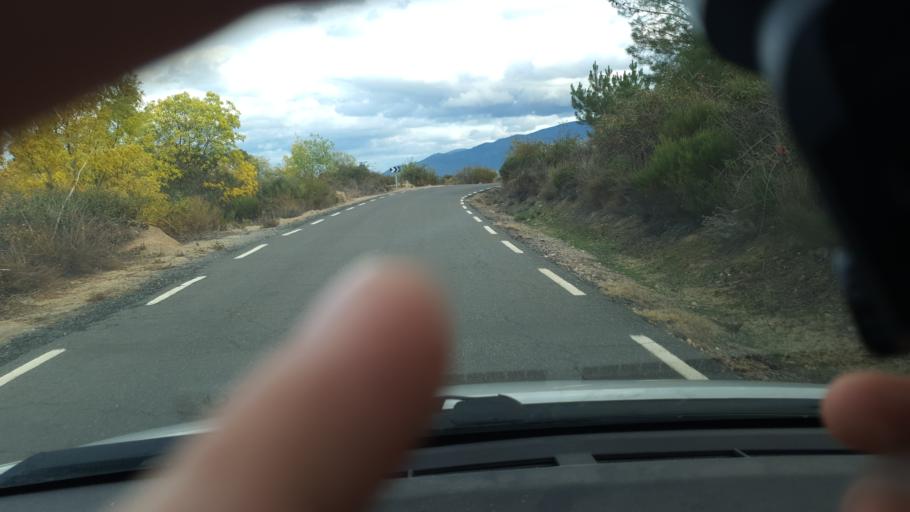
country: ES
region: Castille and Leon
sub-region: Provincia de Avila
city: Burgohondo
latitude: 40.4109
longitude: -4.8037
